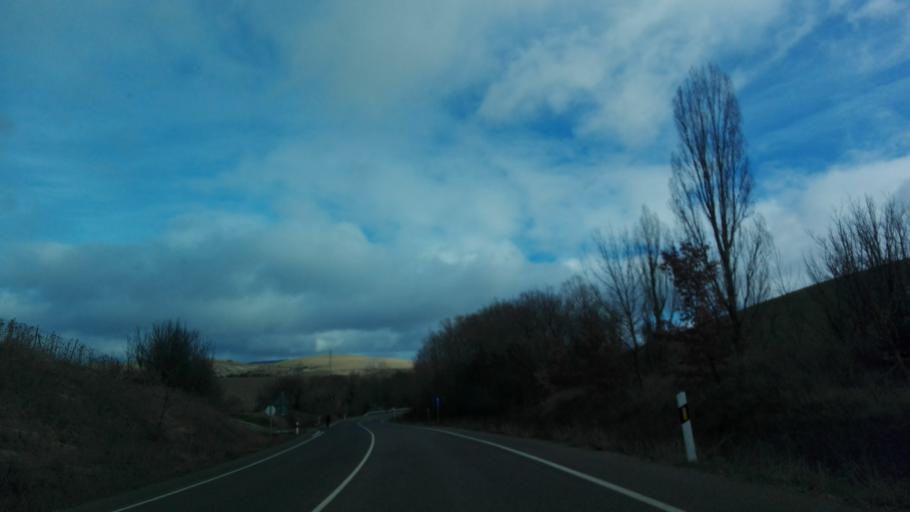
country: ES
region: Navarre
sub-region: Provincia de Navarra
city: Lizoain
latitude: 42.7814
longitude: -1.4610
